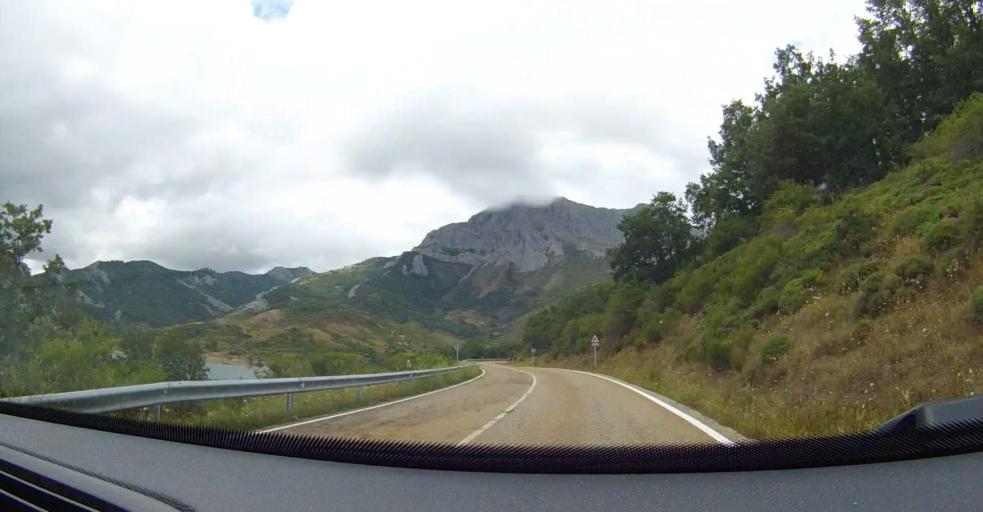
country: ES
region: Castille and Leon
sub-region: Provincia de Leon
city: Puebla de Lillo
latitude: 42.9730
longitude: -5.2586
